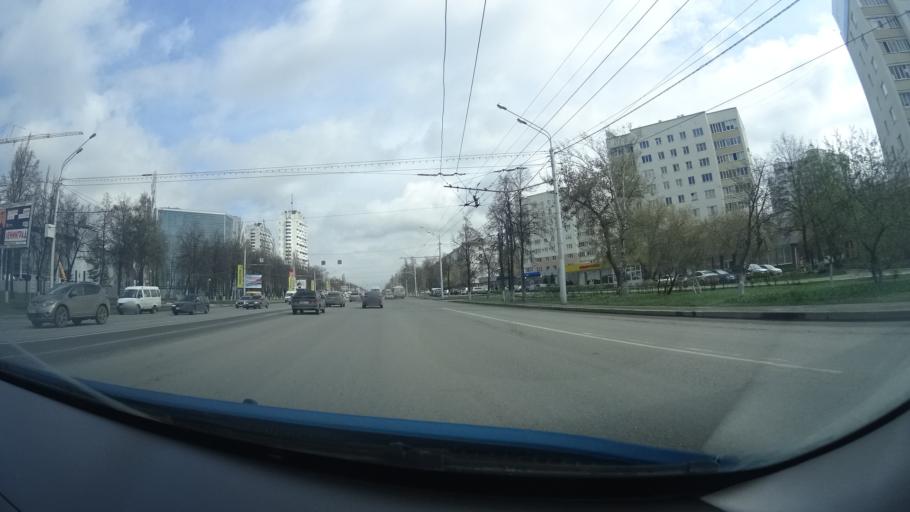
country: RU
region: Bashkortostan
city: Ufa
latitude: 54.7606
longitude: 56.0113
